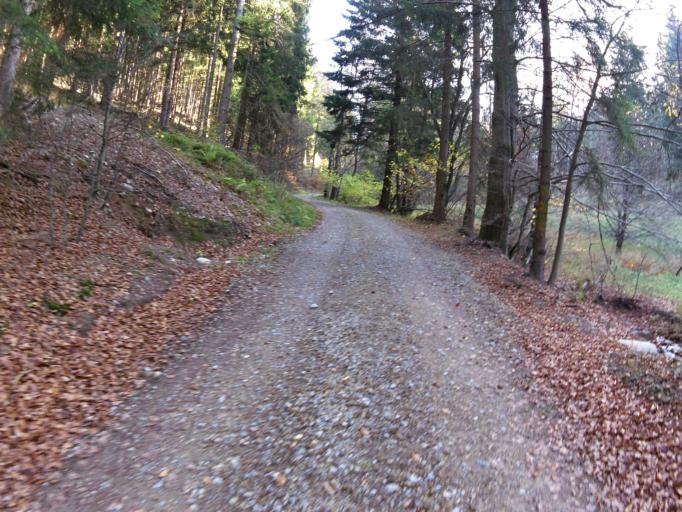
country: DE
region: Thuringia
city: Seebach
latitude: 50.8804
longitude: 10.4051
